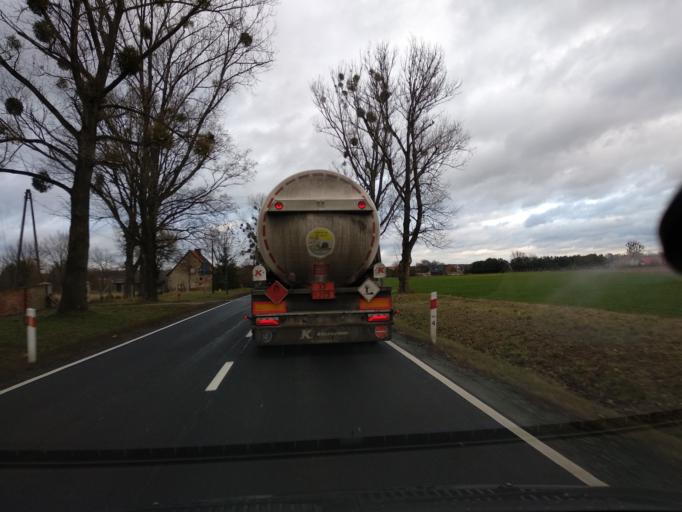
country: PL
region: Lower Silesian Voivodeship
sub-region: Powiat olesnicki
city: Miedzyborz
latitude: 51.3355
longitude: 17.5822
